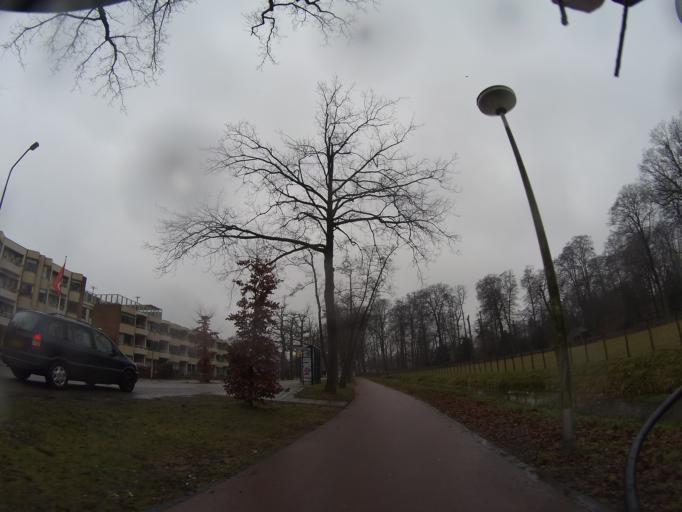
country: NL
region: Utrecht
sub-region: Gemeente Amersfoort
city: Randenbroek
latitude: 52.1506
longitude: 5.4004
